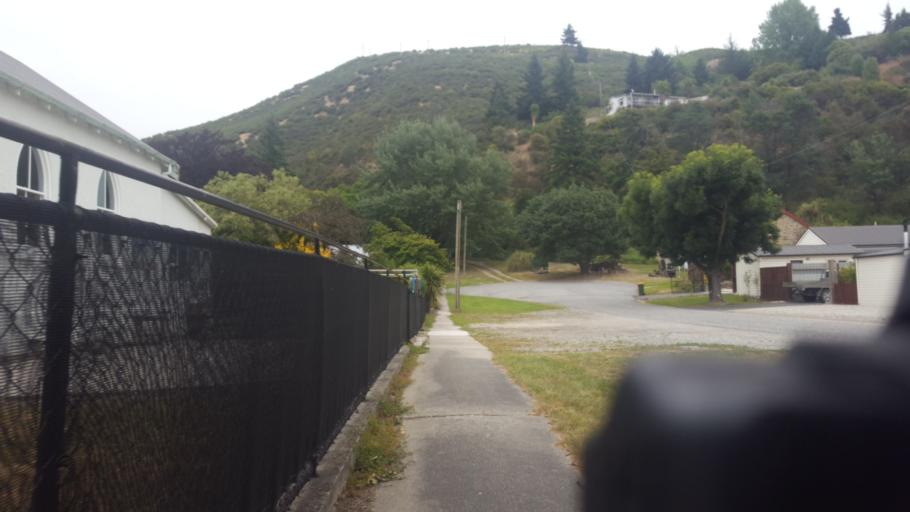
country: NZ
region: Otago
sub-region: Queenstown-Lakes District
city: Kingston
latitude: -45.5395
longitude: 169.3128
